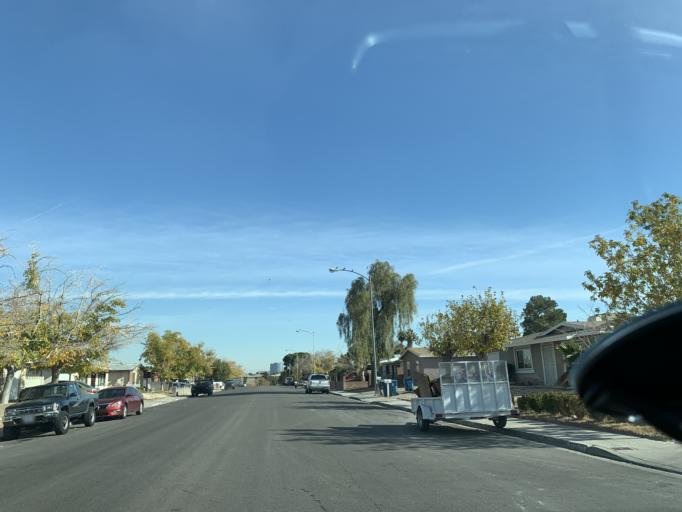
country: US
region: Nevada
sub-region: Clark County
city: Spring Valley
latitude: 36.1104
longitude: -115.2292
